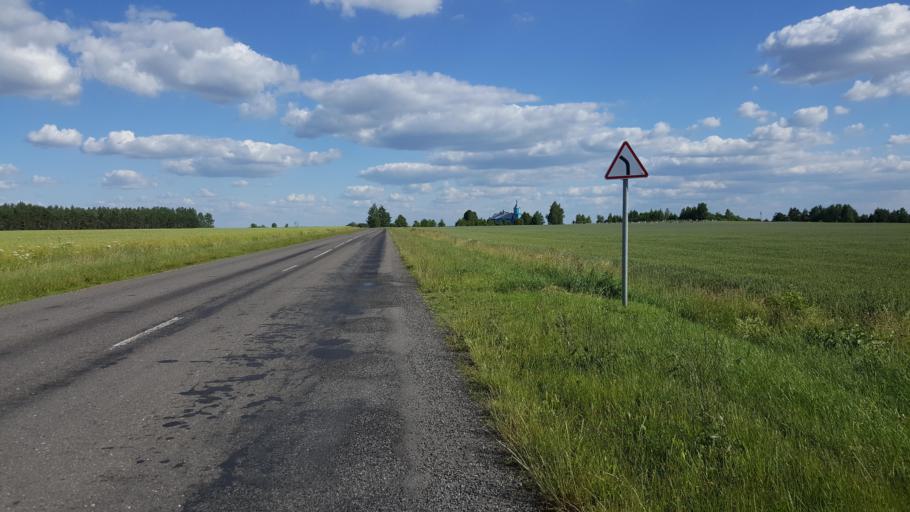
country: BY
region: Brest
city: Kamyanyets
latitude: 52.4495
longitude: 23.7311
